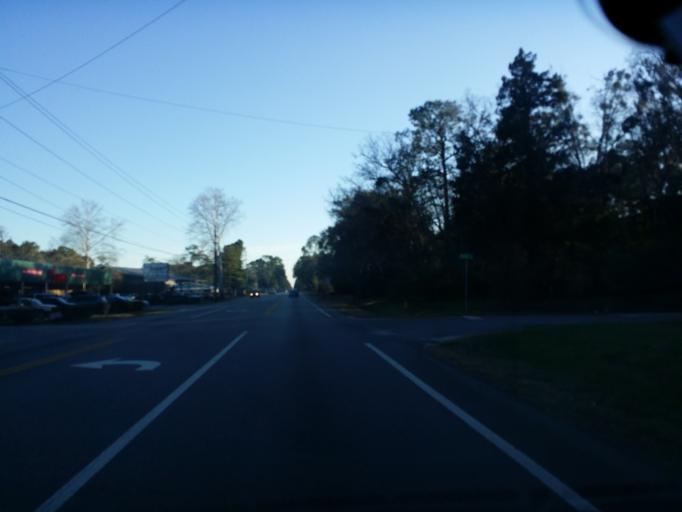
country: US
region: Florida
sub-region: Leon County
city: Woodville
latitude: 30.3180
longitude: -84.2484
